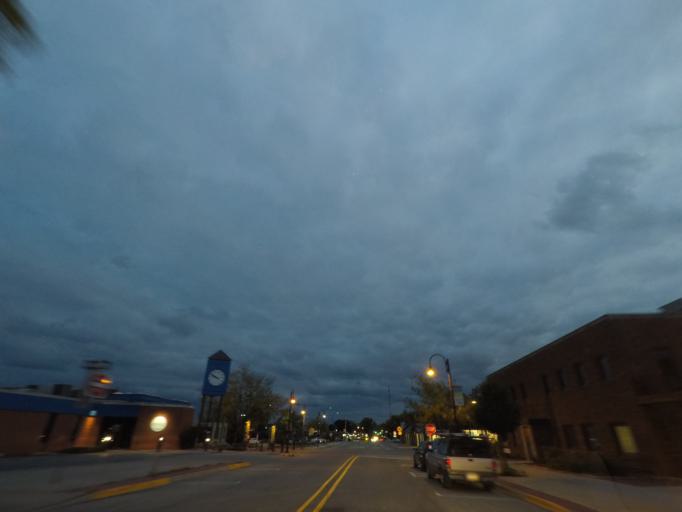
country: US
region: Iowa
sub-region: Story County
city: Ames
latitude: 42.0255
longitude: -93.6170
